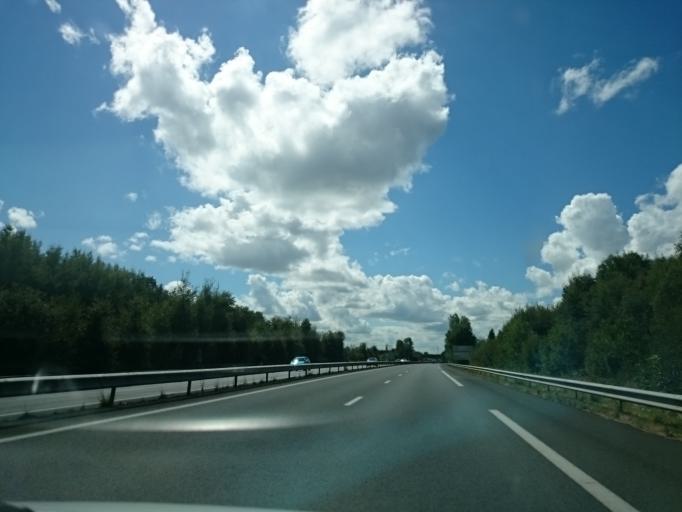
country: FR
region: Pays de la Loire
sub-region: Departement de la Sarthe
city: Parce-sur-Sarthe
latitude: 47.7865
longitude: -0.1886
